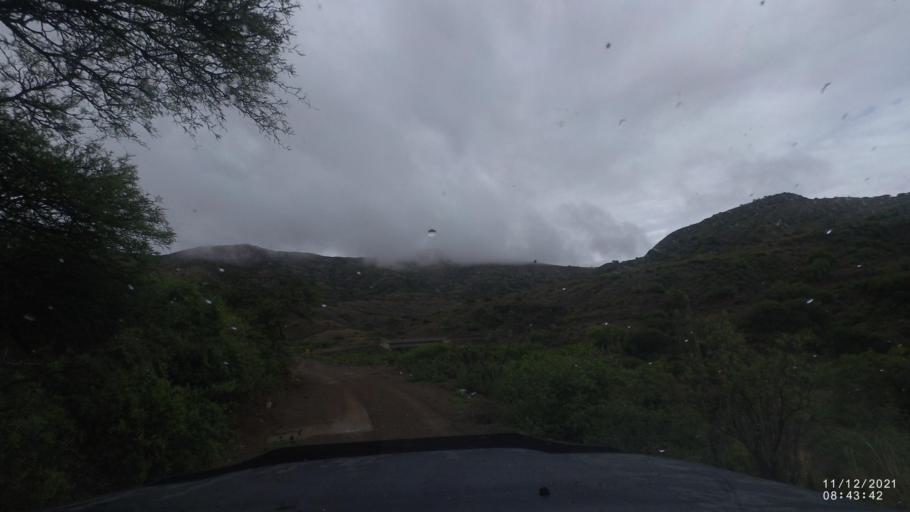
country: BO
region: Cochabamba
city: Tarata
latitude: -17.9132
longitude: -65.9378
